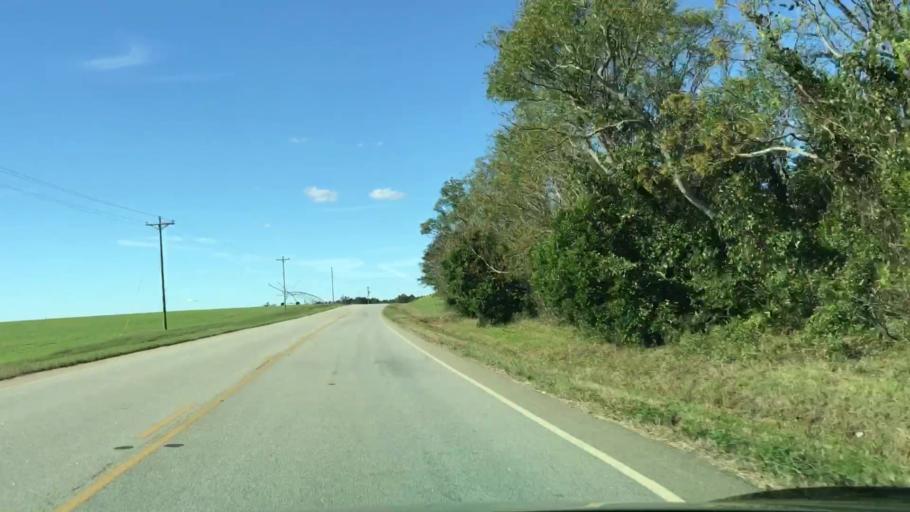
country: US
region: Georgia
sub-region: Jefferson County
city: Louisville
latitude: 33.0762
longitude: -82.4110
